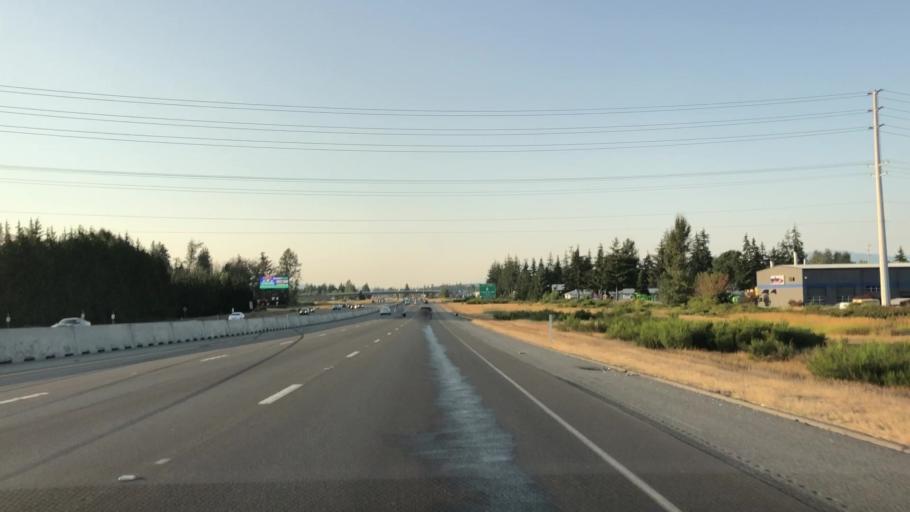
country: US
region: Washington
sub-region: Snohomish County
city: Smokey Point
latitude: 48.1293
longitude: -122.1854
